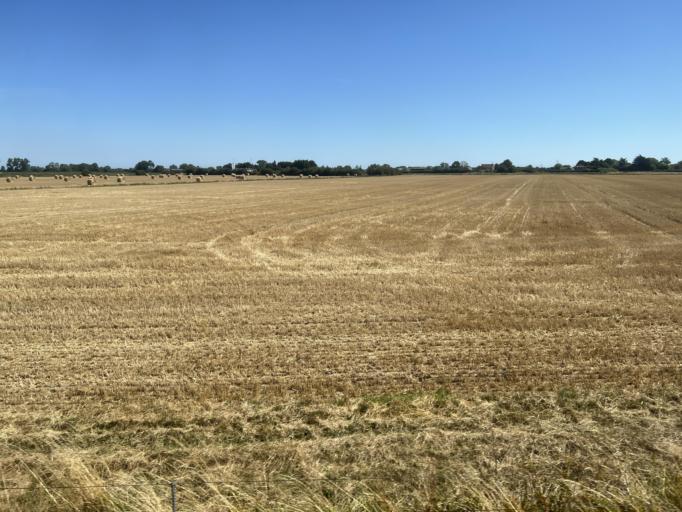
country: GB
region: England
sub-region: Lincolnshire
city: Wainfleet All Saints
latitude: 53.1276
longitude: 0.1956
